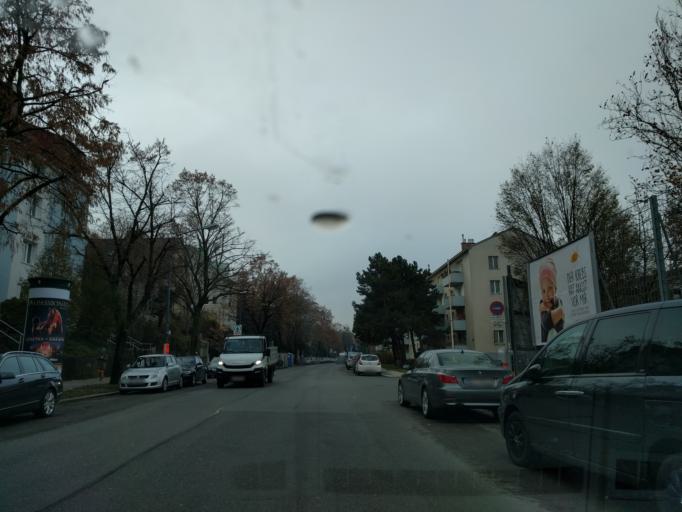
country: AT
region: Vienna
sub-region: Wien Stadt
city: Vienna
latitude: 48.2423
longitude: 16.3248
